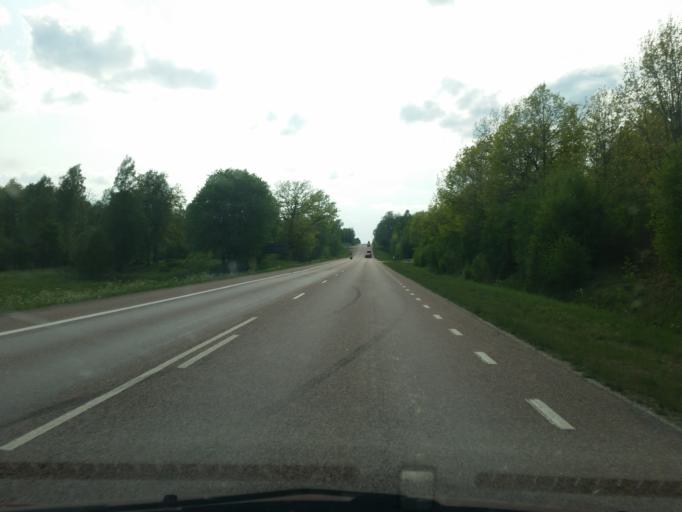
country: SE
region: Vaestra Goetaland
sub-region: Boras Kommun
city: Dalsjofors
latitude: 57.8056
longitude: 13.1931
